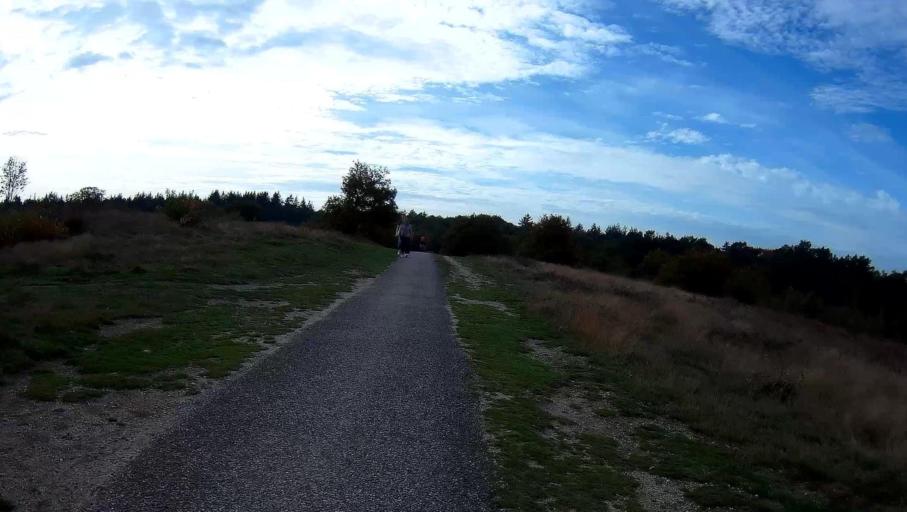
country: NL
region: Gelderland
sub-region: Gemeente Ede
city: Ede
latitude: 52.0463
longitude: 5.6970
